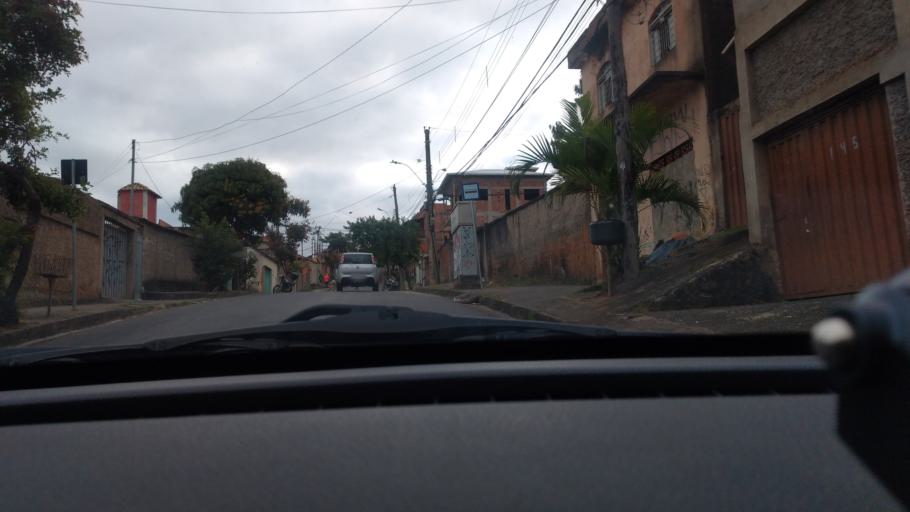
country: BR
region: Minas Gerais
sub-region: Santa Luzia
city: Santa Luzia
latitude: -19.8151
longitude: -43.9377
